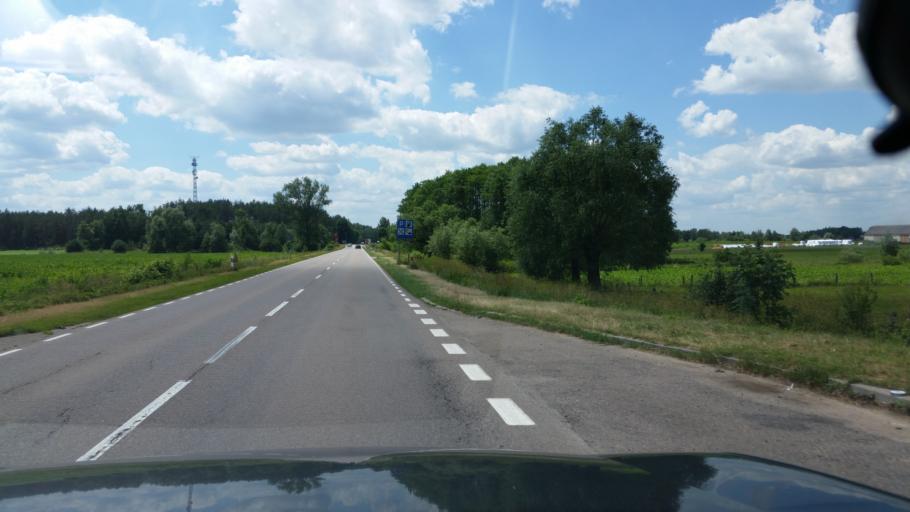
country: PL
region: Podlasie
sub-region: Powiat lomzynski
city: Sniadowo
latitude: 53.0039
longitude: 21.9346
